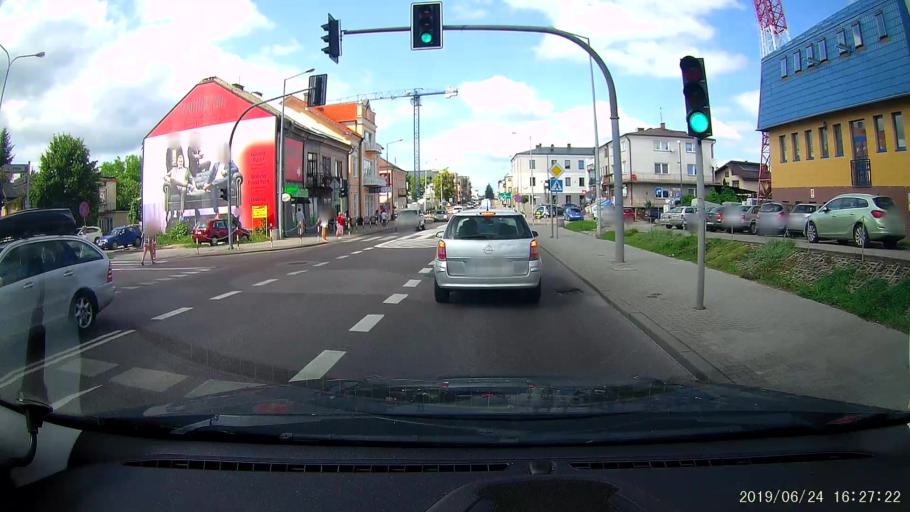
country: PL
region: Lublin Voivodeship
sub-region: Powiat tomaszowski
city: Tomaszow Lubelski
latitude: 50.4503
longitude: 23.4177
